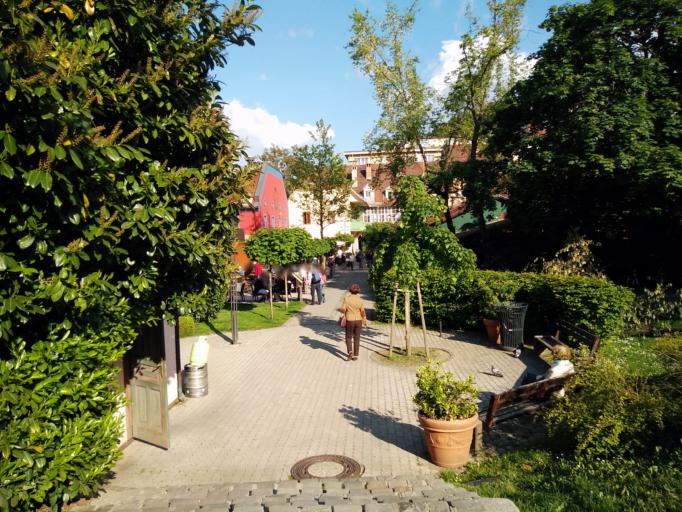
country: SI
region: Ljubljana
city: Ljubljana
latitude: 46.0516
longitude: 14.5043
